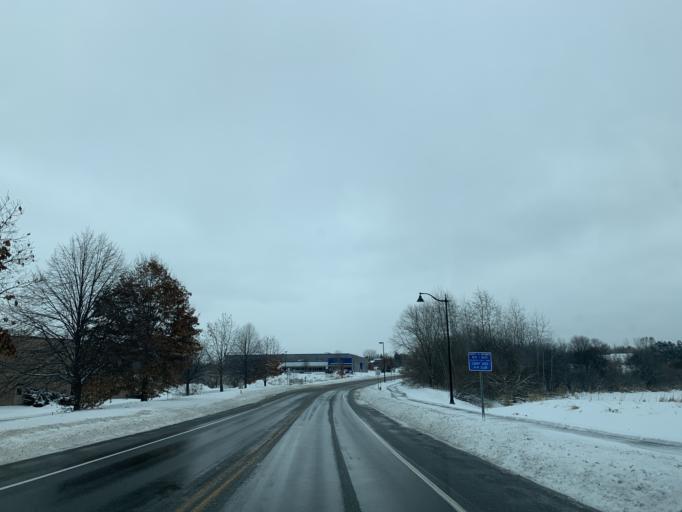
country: US
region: Minnesota
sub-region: Ramsey County
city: North Saint Paul
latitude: 45.0252
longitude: -92.9702
